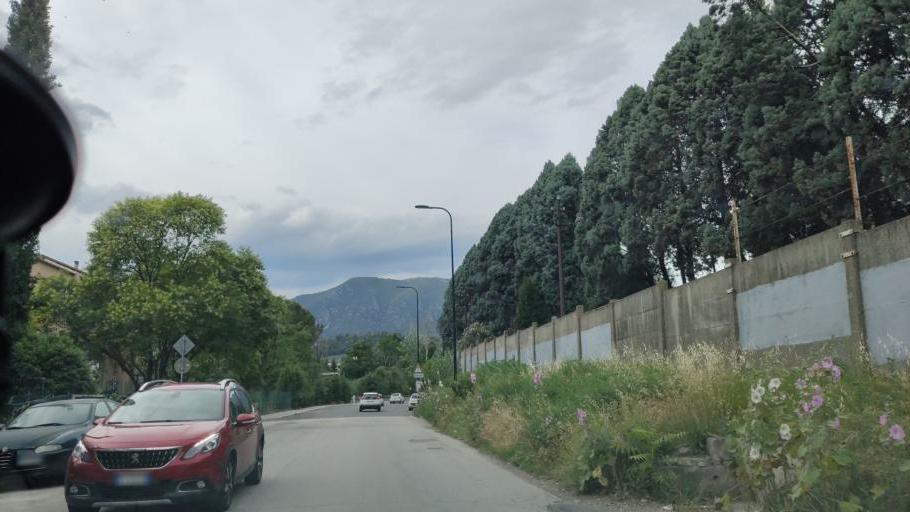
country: IT
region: Umbria
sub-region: Provincia di Terni
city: Terni
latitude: 42.5648
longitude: 12.6591
